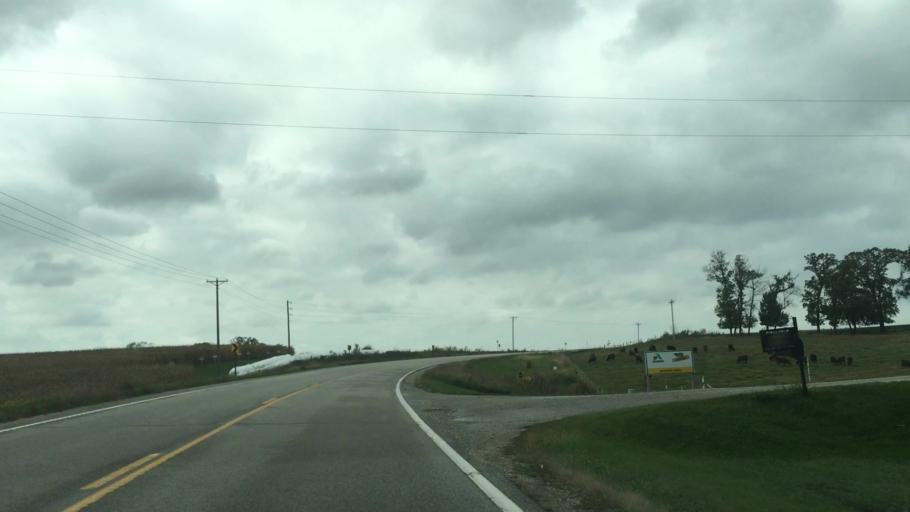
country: US
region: Minnesota
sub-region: Fillmore County
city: Preston
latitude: 43.7318
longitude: -92.0920
